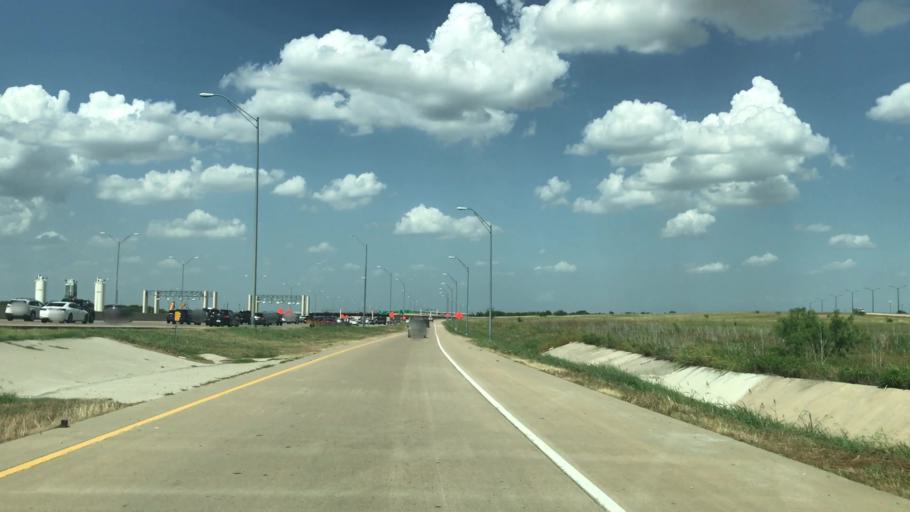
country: US
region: Texas
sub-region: Tarrant County
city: Grapevine
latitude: 32.9246
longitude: -97.0568
